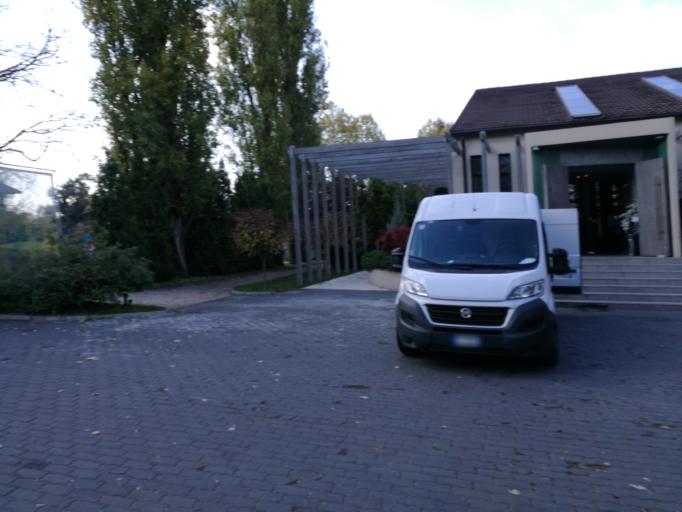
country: RO
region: Bucuresti
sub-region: Municipiul Bucuresti
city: Bucharest
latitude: 44.4754
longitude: 26.0897
